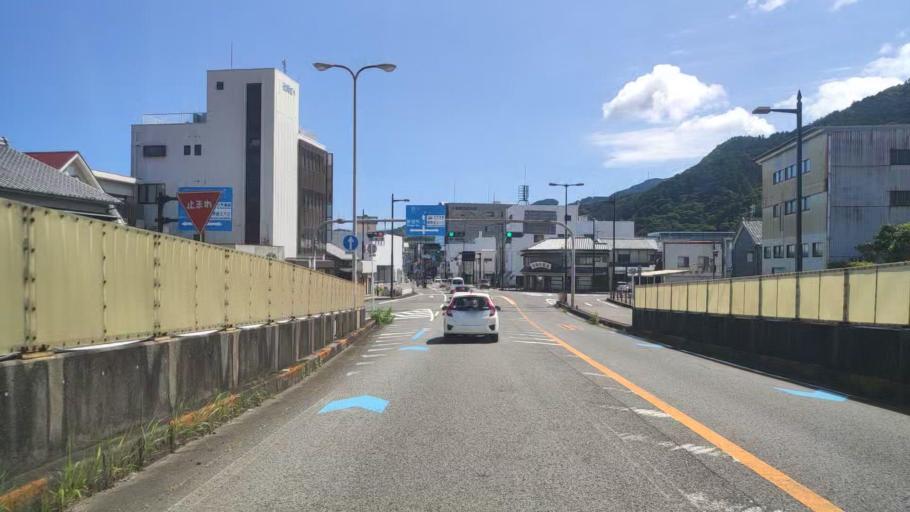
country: JP
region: Wakayama
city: Shingu
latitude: 33.7312
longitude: 135.9870
